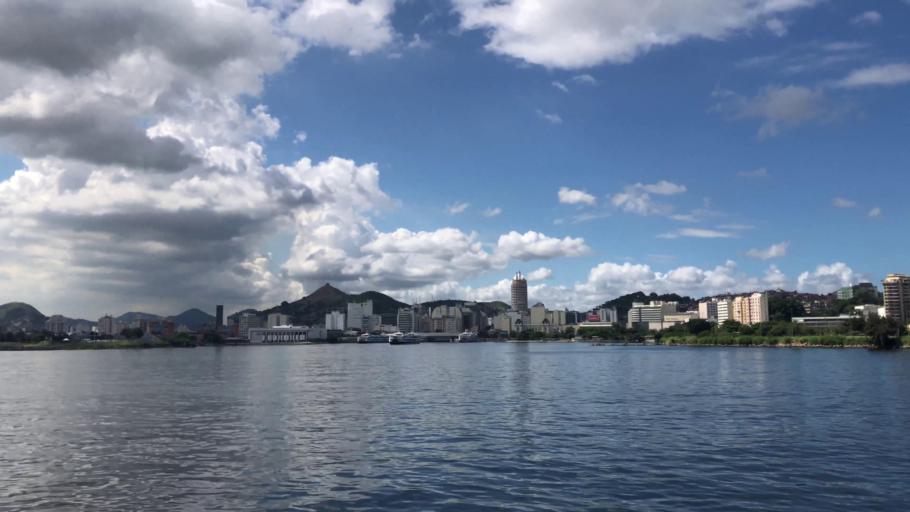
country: BR
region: Rio de Janeiro
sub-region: Niteroi
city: Niteroi
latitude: -22.8943
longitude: -43.1296
